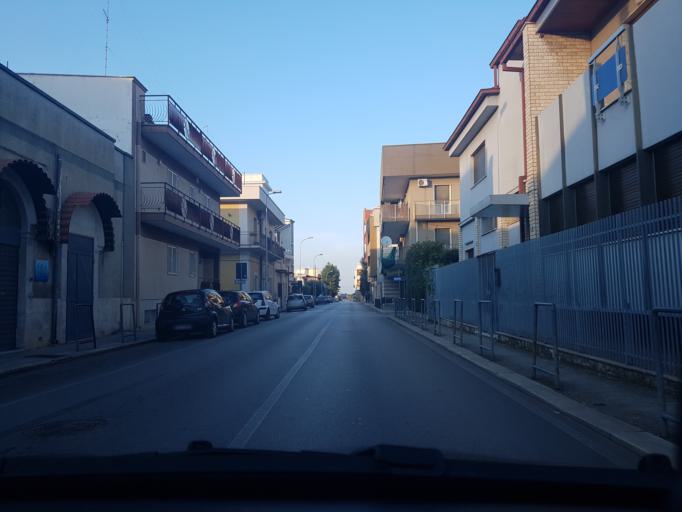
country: IT
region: Apulia
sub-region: Provincia di Bari
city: Bitritto
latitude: 41.0446
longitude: 16.8269
